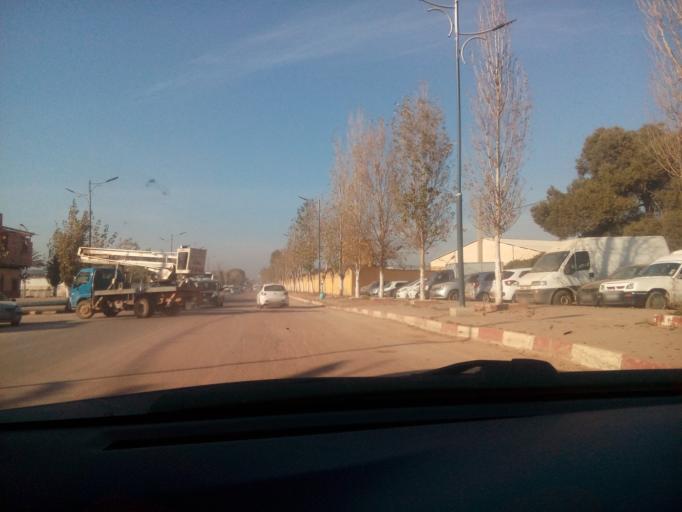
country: DZ
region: Oran
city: Es Senia
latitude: 35.6521
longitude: -0.6134
